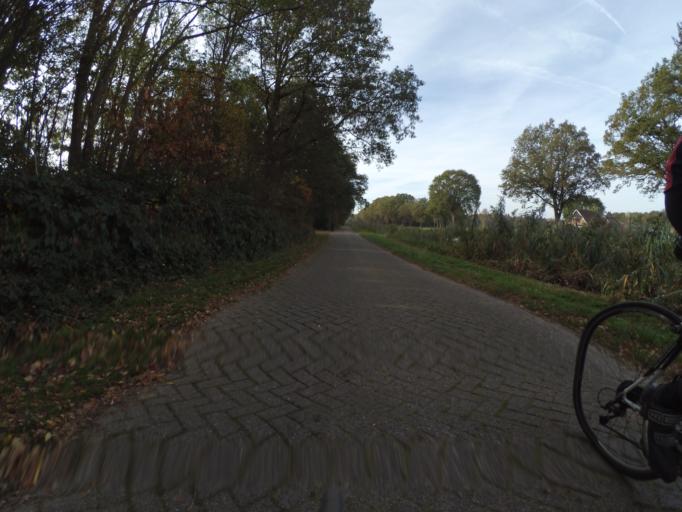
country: NL
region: Overijssel
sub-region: Gemeente Deventer
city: Schalkhaar
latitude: 52.3091
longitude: 6.2591
